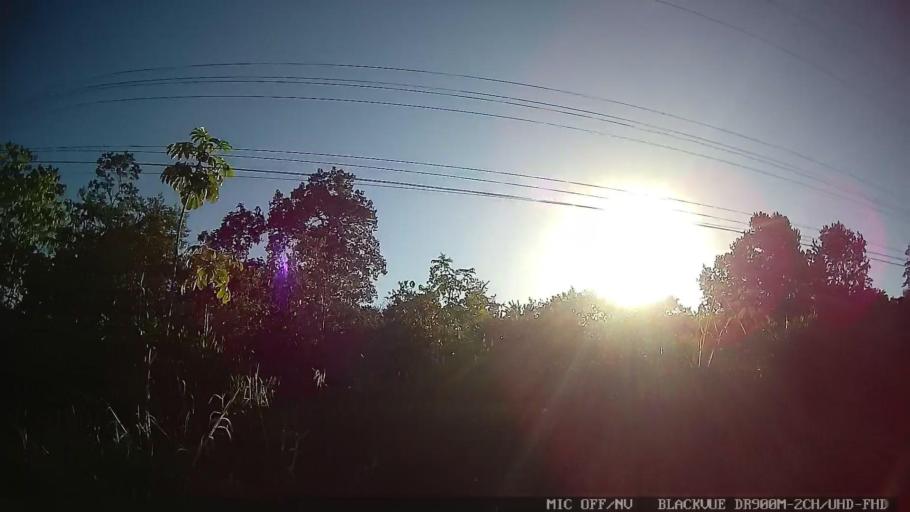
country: BR
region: Sao Paulo
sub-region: Itanhaem
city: Itanhaem
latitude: -24.2037
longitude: -46.8644
